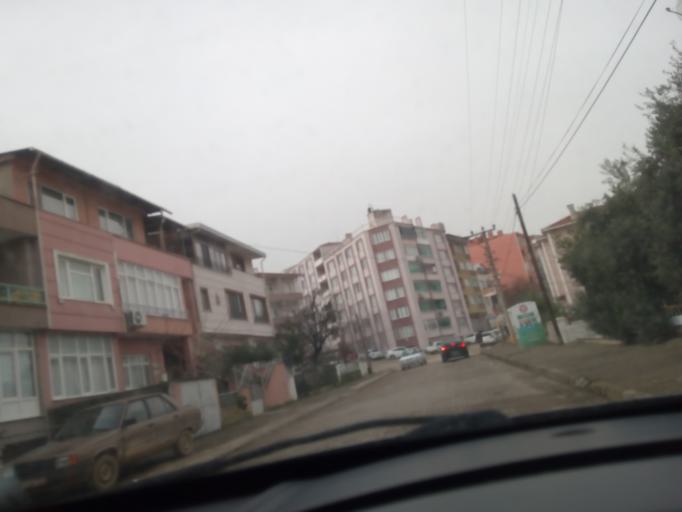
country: TR
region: Balikesir
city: Susurluk
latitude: 39.9183
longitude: 28.1520
